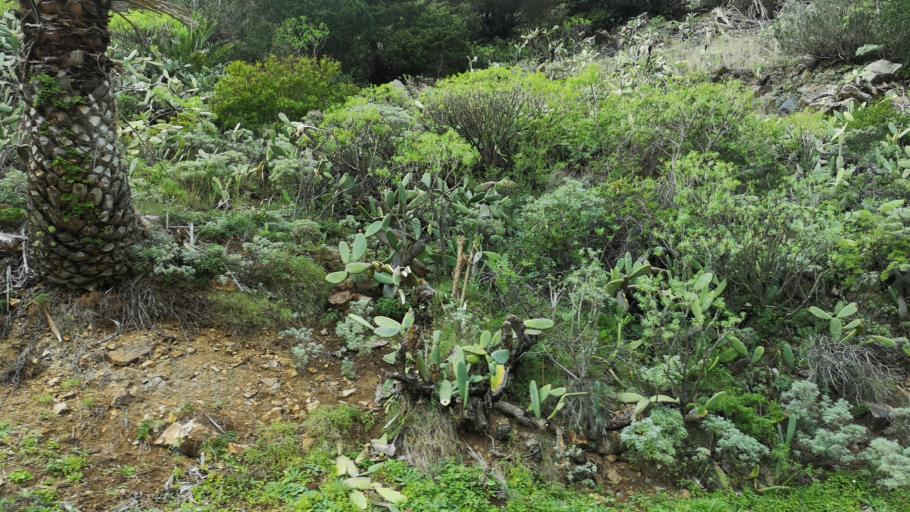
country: ES
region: Canary Islands
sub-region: Provincia de Santa Cruz de Tenerife
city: Vallehermosa
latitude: 28.1715
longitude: -17.2787
